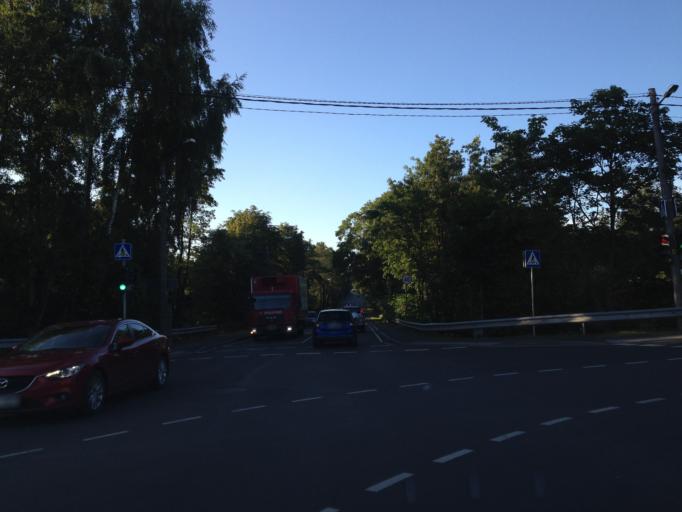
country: EE
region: Harju
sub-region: Saue vald
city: Laagri
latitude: 59.3870
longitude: 24.6406
